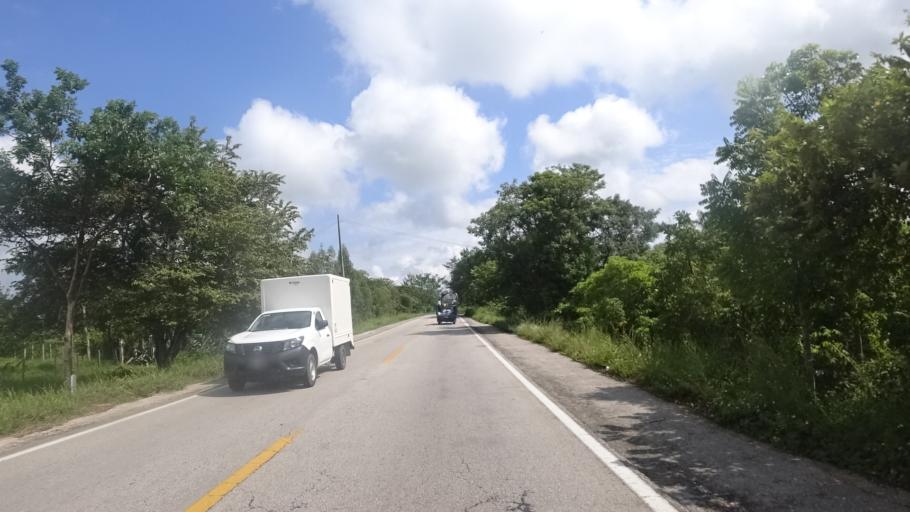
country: MX
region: Chiapas
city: Palenque
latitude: 17.5996
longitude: -92.0291
